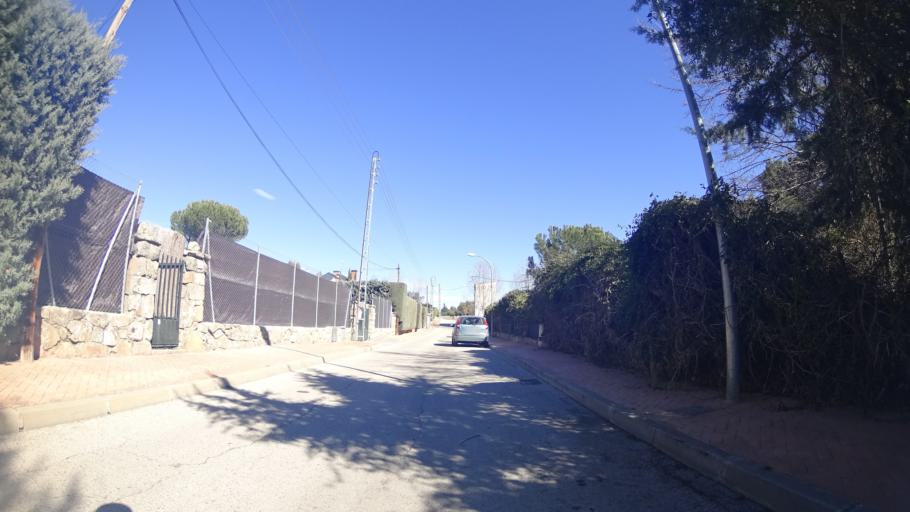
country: ES
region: Madrid
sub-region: Provincia de Madrid
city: Colmenarejo
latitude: 40.5674
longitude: -4.0102
